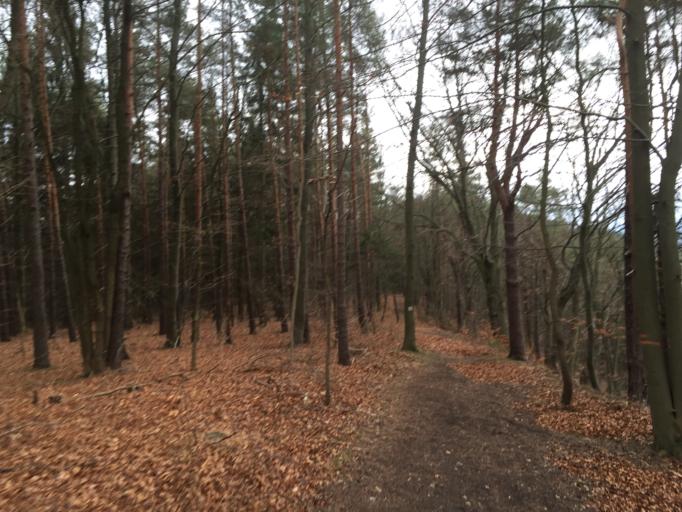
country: DE
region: Thuringia
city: Bad Blankenburg
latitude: 50.6948
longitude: 11.2738
